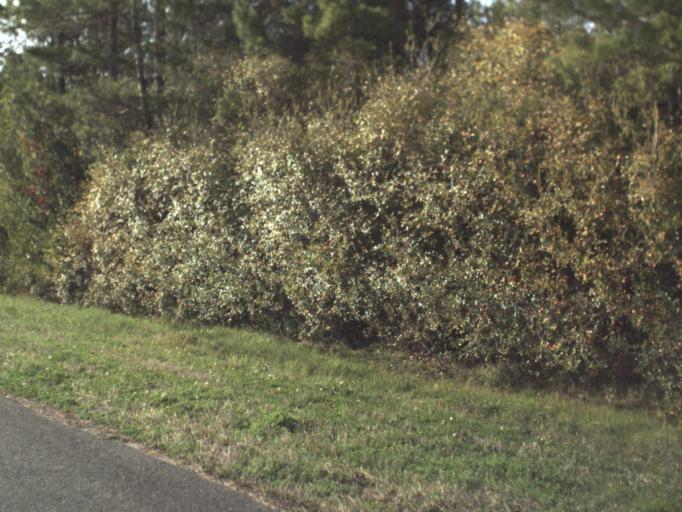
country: US
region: Florida
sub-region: Bay County
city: Youngstown
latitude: 30.4359
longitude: -85.4481
